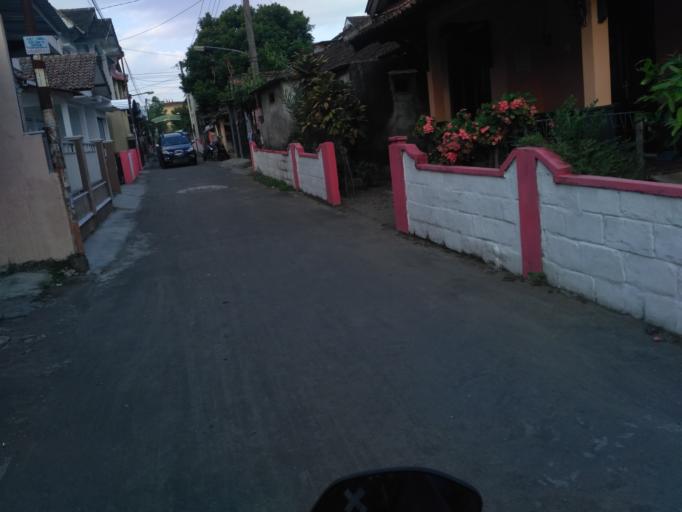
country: ID
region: Daerah Istimewa Yogyakarta
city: Depok
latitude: -7.7639
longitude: 110.4053
